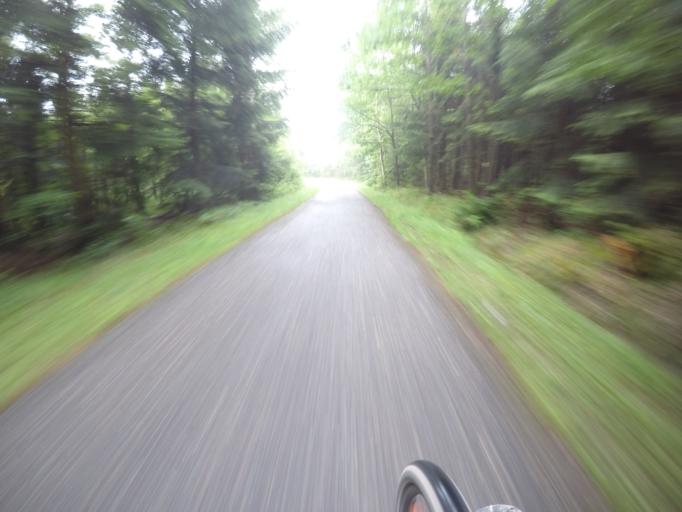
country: DE
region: Baden-Wuerttemberg
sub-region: Regierungsbezirk Stuttgart
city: Sindelfingen
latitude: 48.7194
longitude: 9.0538
